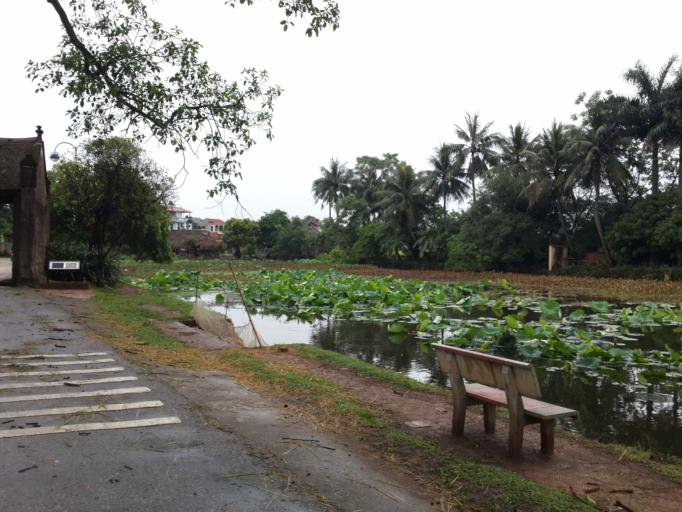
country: VN
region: Ha Noi
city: Son Tay
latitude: 21.1572
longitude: 105.4727
